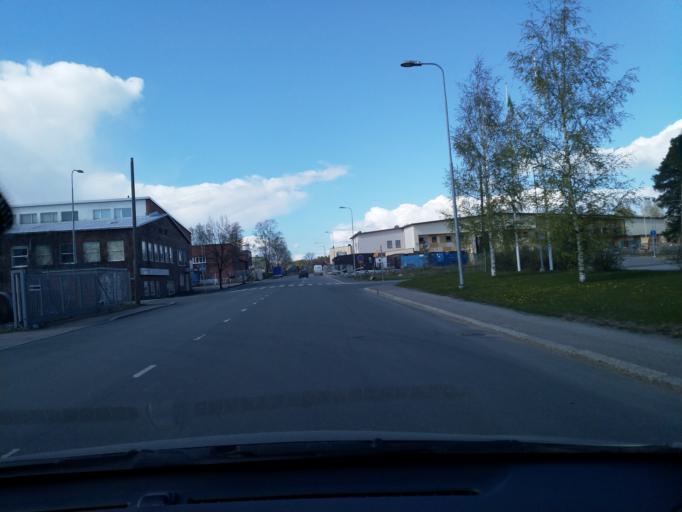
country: FI
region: Pirkanmaa
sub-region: Tampere
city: Tampere
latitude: 61.4806
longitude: 23.7896
